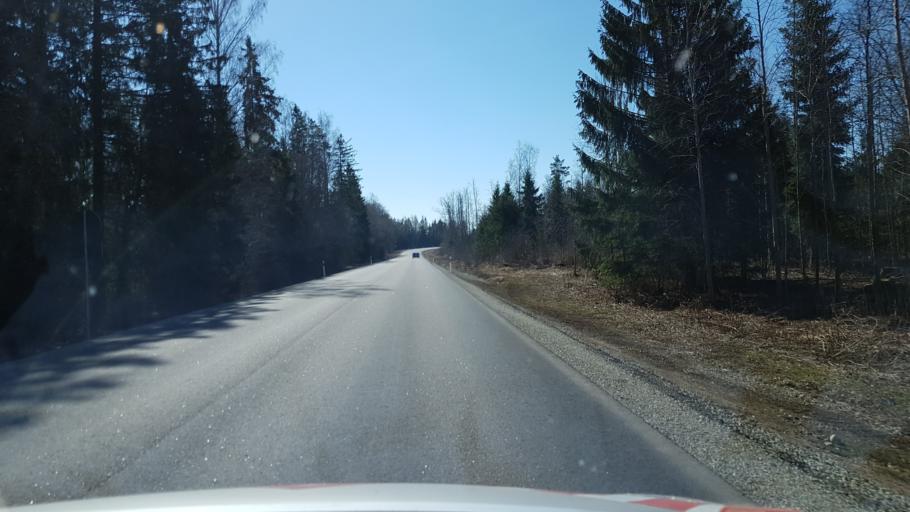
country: EE
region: Laeaene-Virumaa
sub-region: Vinni vald
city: Vinni
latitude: 59.1226
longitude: 26.6171
